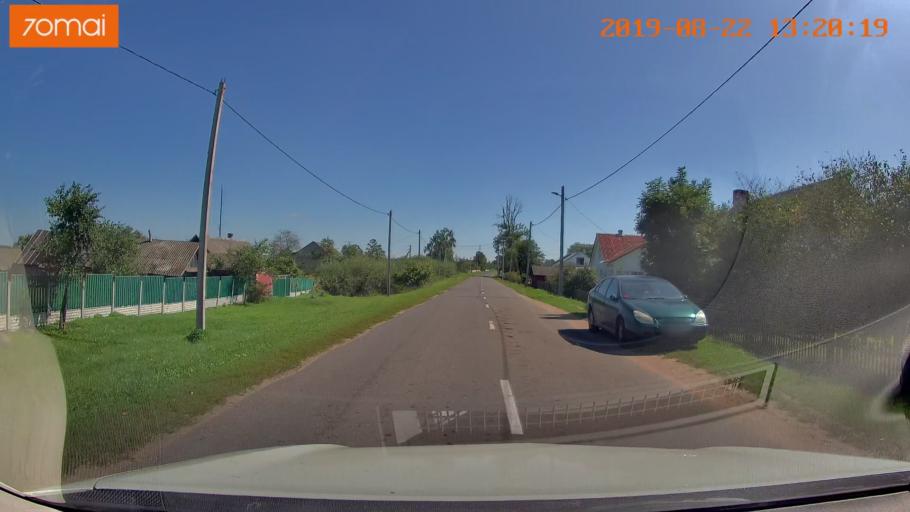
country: BY
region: Minsk
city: Urechcha
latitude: 53.2303
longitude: 27.9657
